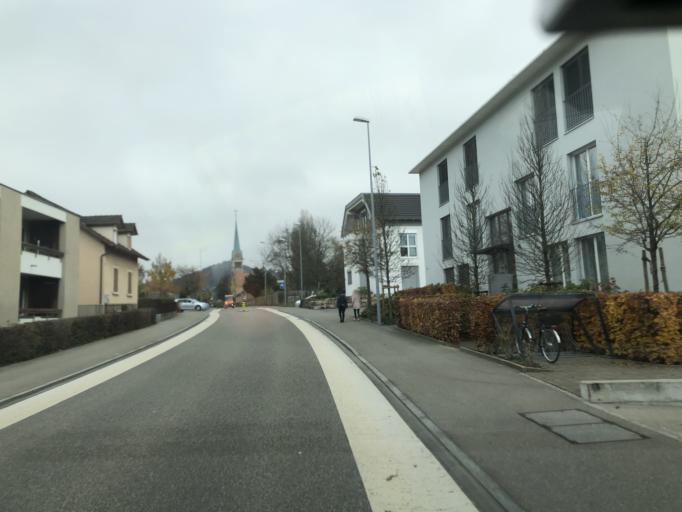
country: CH
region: Aargau
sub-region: Bezirk Baden
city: Wettingen
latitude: 47.4685
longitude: 8.3265
